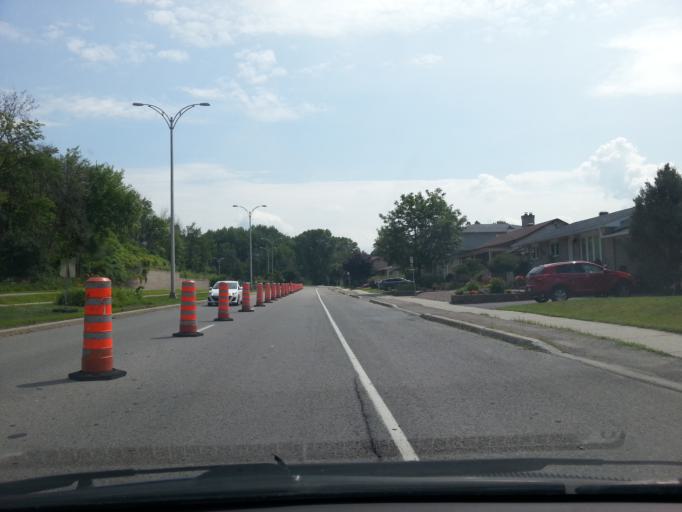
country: CA
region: Quebec
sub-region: Outaouais
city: Gatineau
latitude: 45.4970
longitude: -75.6663
